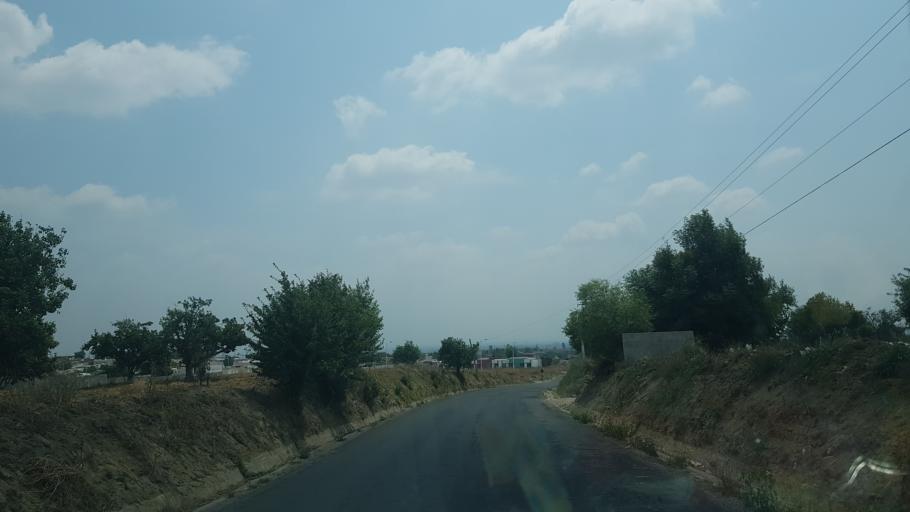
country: MX
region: Puebla
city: Huejotzingo
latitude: 19.1370
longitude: -98.4188
